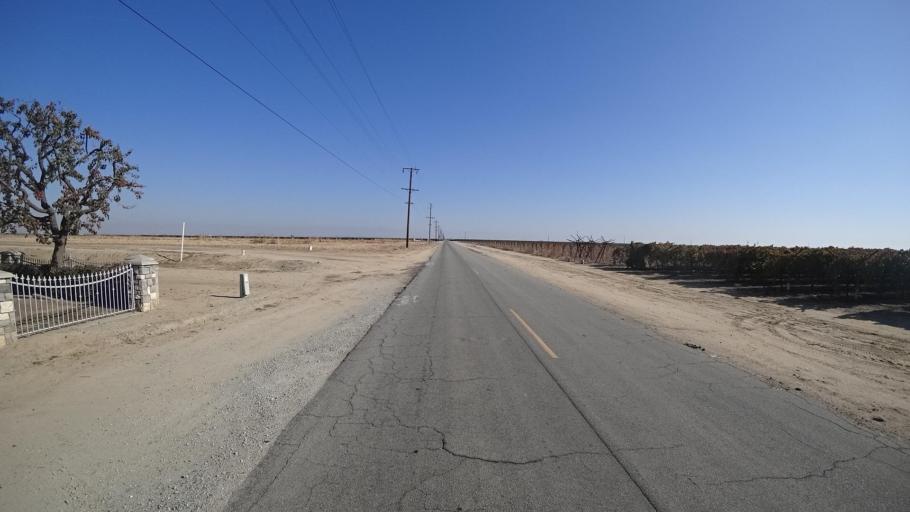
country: US
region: California
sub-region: Kern County
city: McFarland
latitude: 35.7035
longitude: -119.1829
